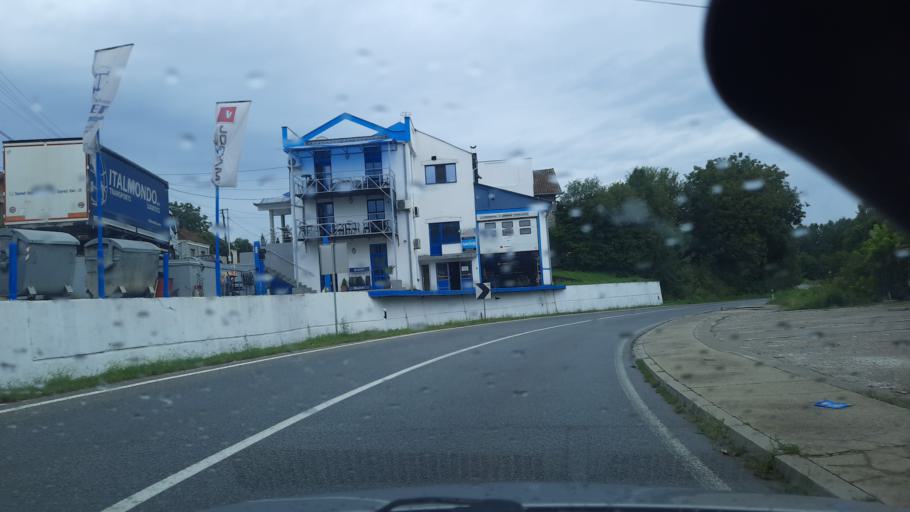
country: RS
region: Central Serbia
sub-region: Sumadijski Okrug
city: Knic
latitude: 43.8951
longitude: 20.7712
